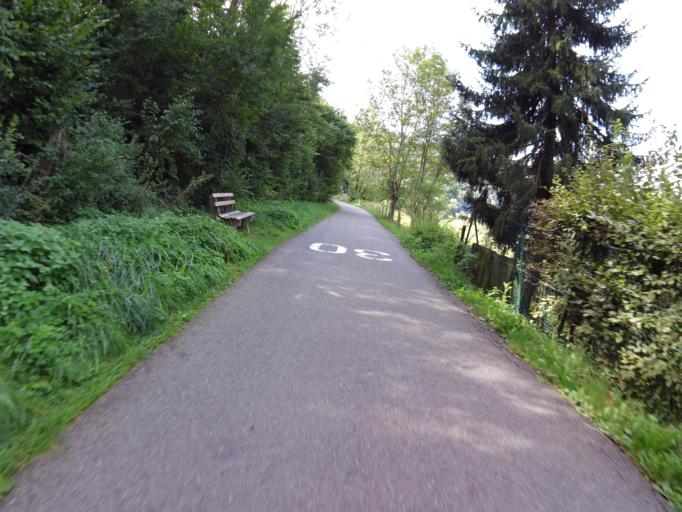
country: DE
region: Baden-Wuerttemberg
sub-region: Karlsruhe Region
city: Horb am Neckar
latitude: 48.4472
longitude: 8.7194
